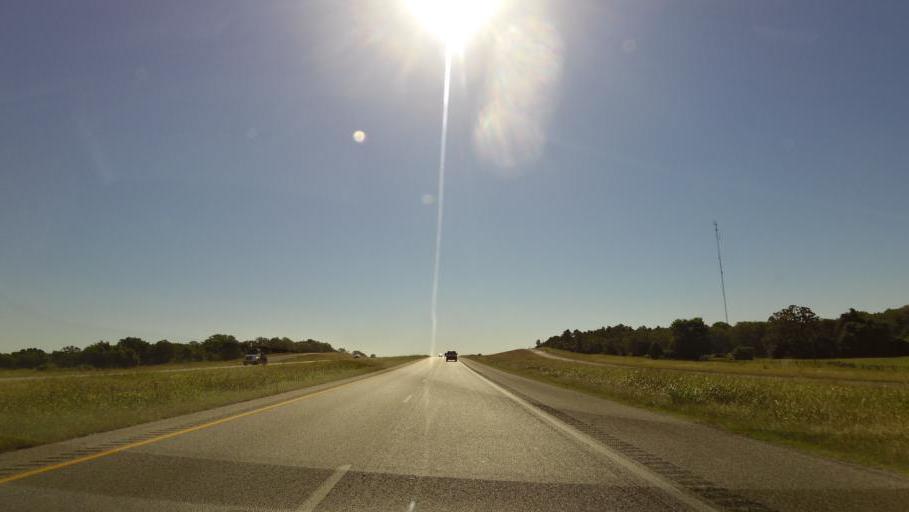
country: US
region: Texas
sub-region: Caldwell County
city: Luling
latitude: 29.6536
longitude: -97.5604
